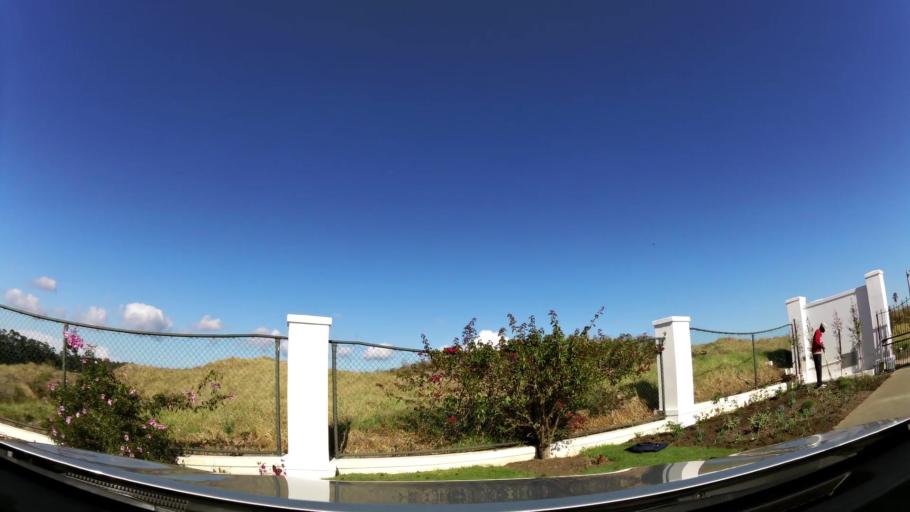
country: ZA
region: Western Cape
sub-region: Eden District Municipality
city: George
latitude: -33.9673
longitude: 22.4076
